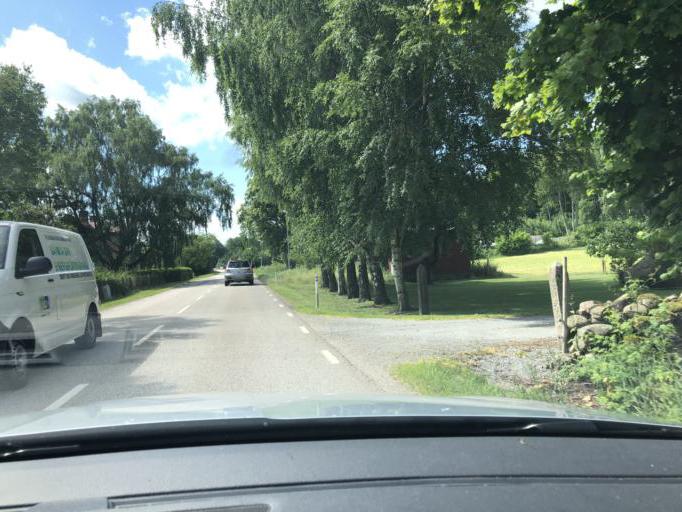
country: SE
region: Blekinge
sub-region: Solvesborgs Kommun
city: Soelvesborg
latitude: 56.1040
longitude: 14.6186
